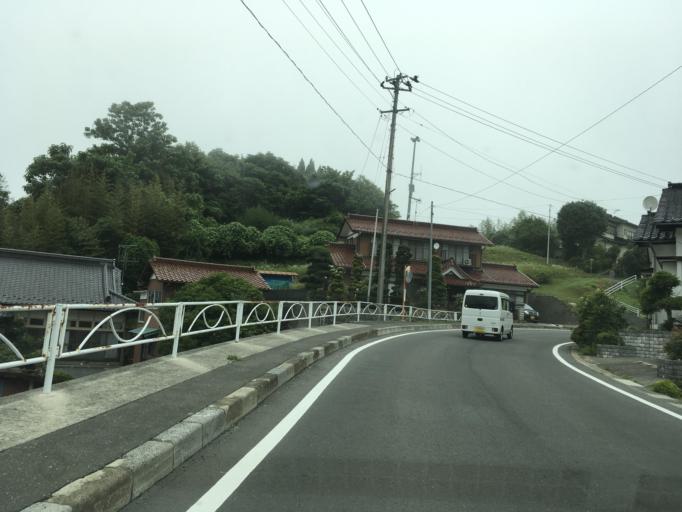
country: JP
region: Iwate
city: Ofunato
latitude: 38.8982
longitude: 141.6415
